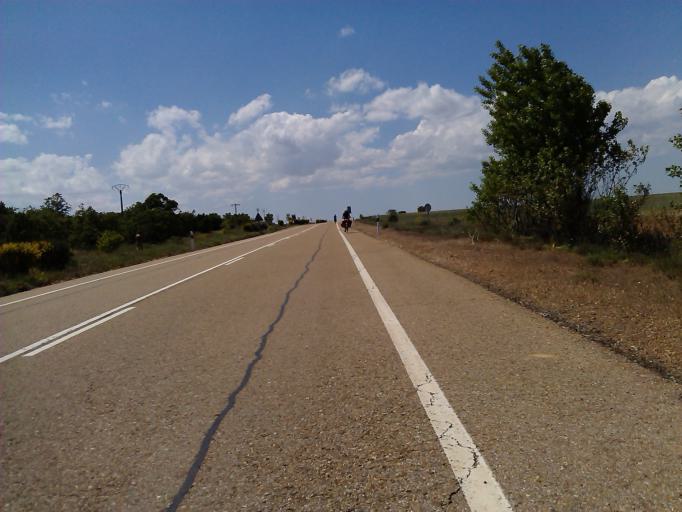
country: ES
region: Castille and Leon
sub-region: Provincia de Palencia
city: Ledigos
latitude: 42.3443
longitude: -4.8461
